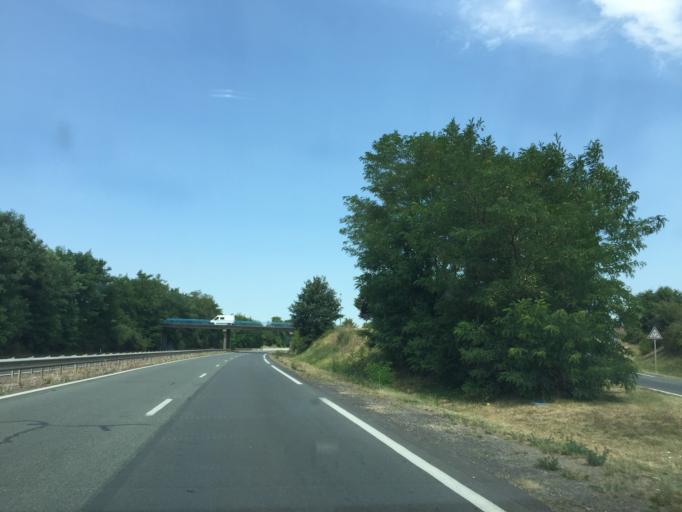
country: FR
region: Poitou-Charentes
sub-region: Departement de la Vienne
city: Biard
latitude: 46.5611
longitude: 0.3027
